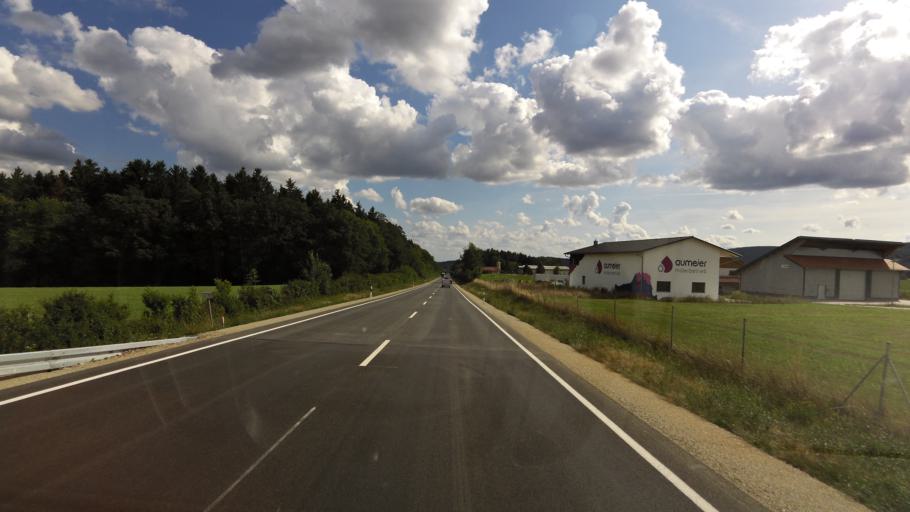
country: DE
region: Bavaria
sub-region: Lower Bavaria
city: Loitzendorf
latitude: 49.0836
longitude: 12.6400
